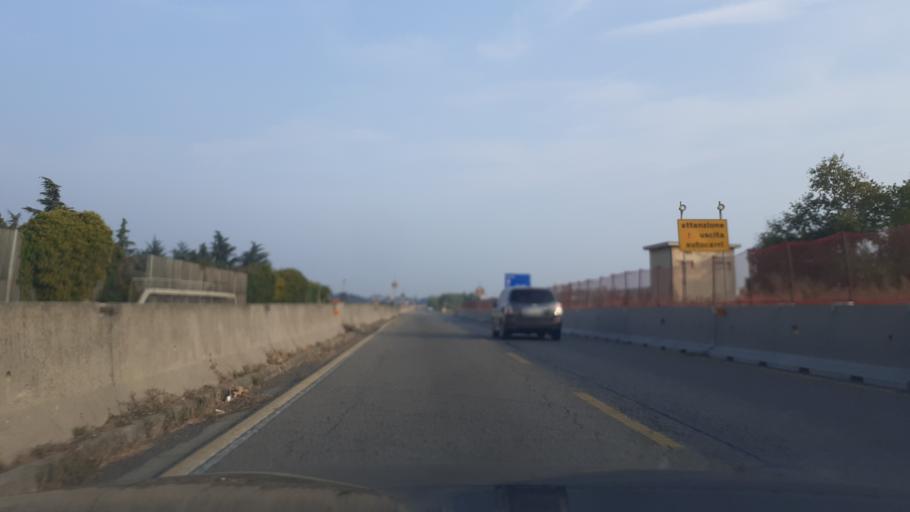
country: IT
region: Lombardy
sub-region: Citta metropolitana di Milano
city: Novate Milanese
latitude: 45.5468
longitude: 9.1481
